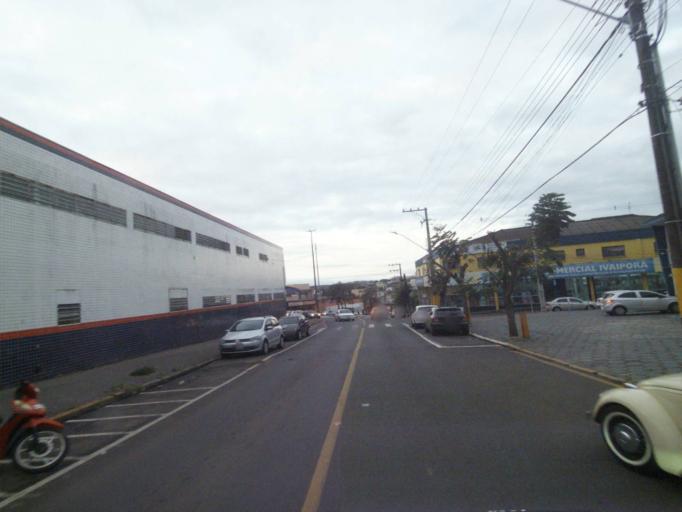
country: BR
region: Parana
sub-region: Telemaco Borba
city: Telemaco Borba
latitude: -24.3243
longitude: -50.6208
